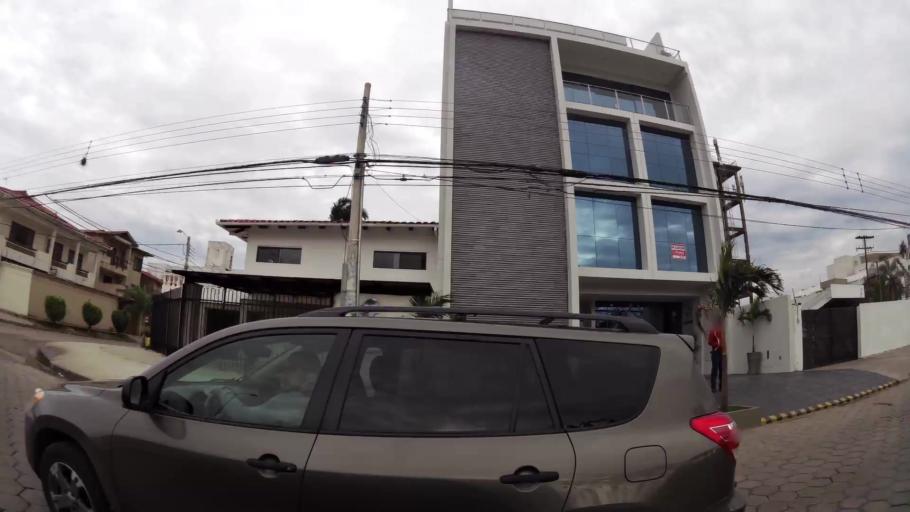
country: BO
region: Santa Cruz
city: Santa Cruz de la Sierra
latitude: -17.7561
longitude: -63.1658
